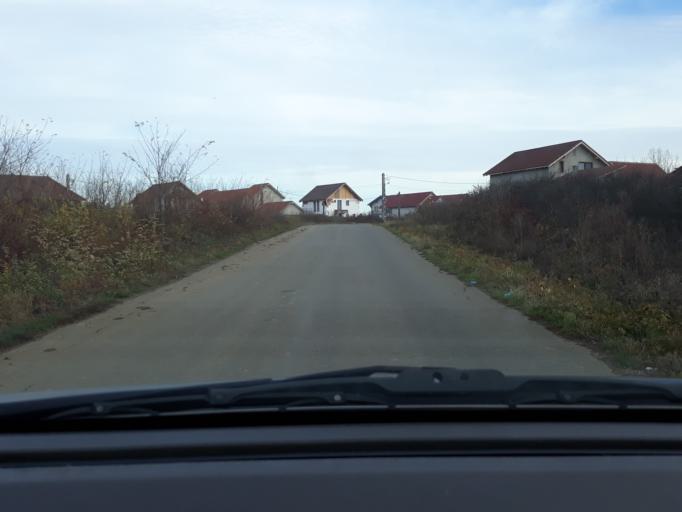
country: RO
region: Bihor
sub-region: Comuna Sanmartin
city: Sanmartin
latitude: 47.0191
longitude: 22.0085
